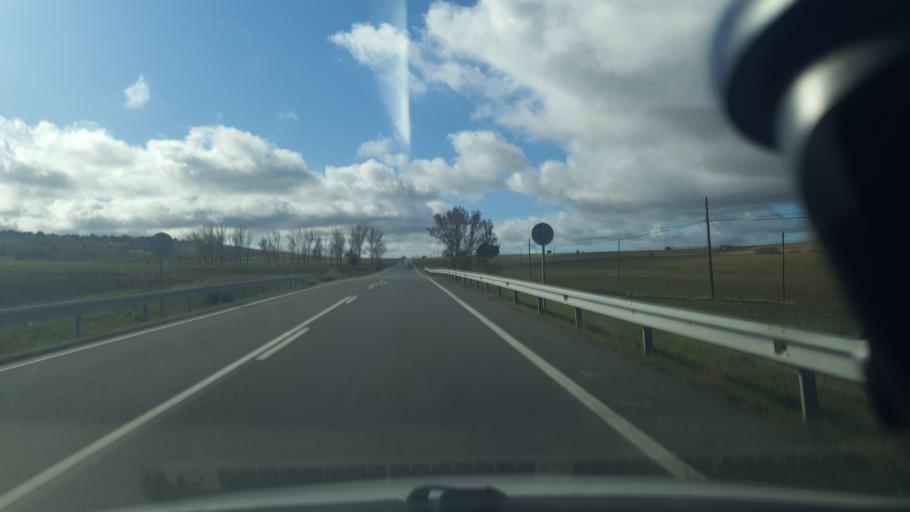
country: ES
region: Castille and Leon
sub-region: Provincia de Segovia
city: Ituero y Lama
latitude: 40.7926
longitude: -4.3899
